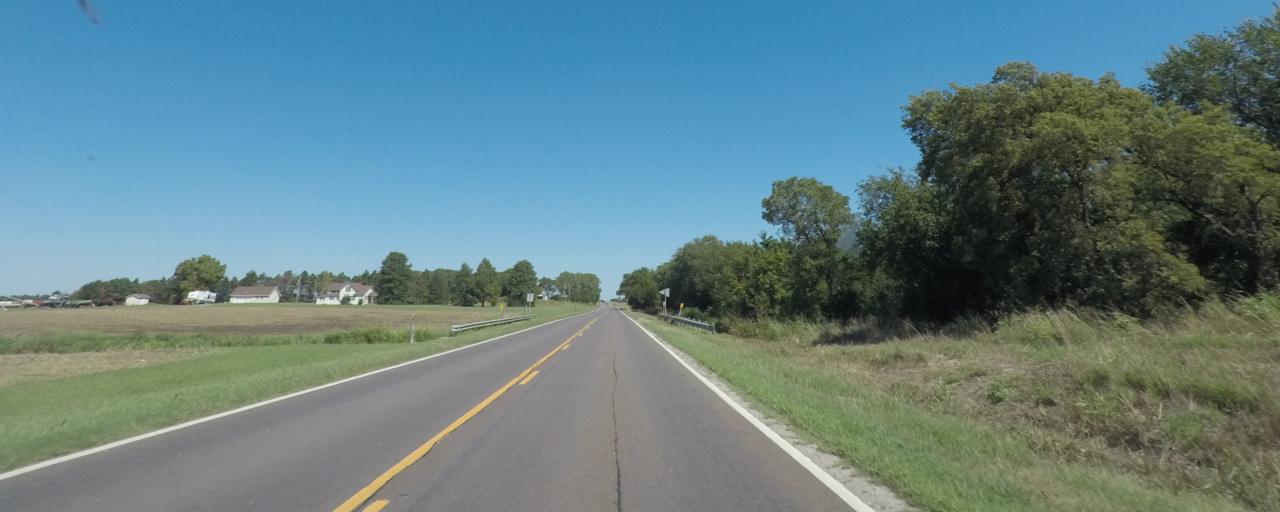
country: US
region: Kansas
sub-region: Sumner County
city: Wellington
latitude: 37.1264
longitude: -97.4016
